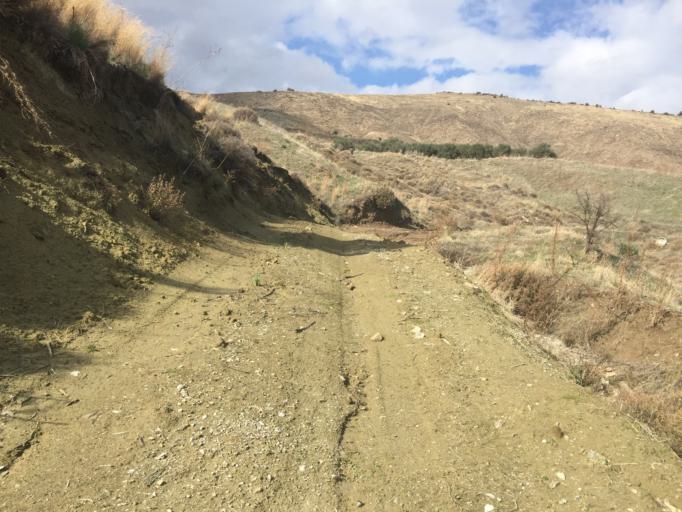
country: CY
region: Limassol
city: Pachna
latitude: 34.8732
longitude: 32.6578
